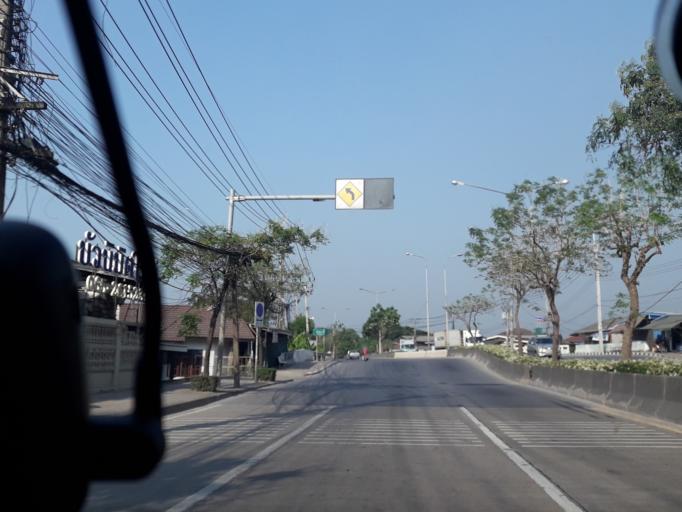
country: TH
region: Pathum Thani
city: Lam Luk Ka
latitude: 13.8976
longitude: 100.7343
